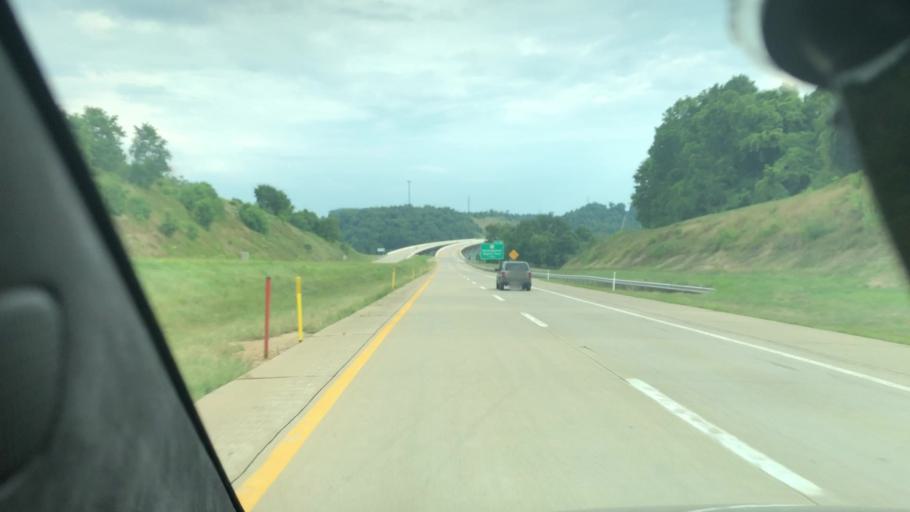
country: US
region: Pennsylvania
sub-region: Washington County
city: Baidland
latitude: 40.2165
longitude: -79.9849
